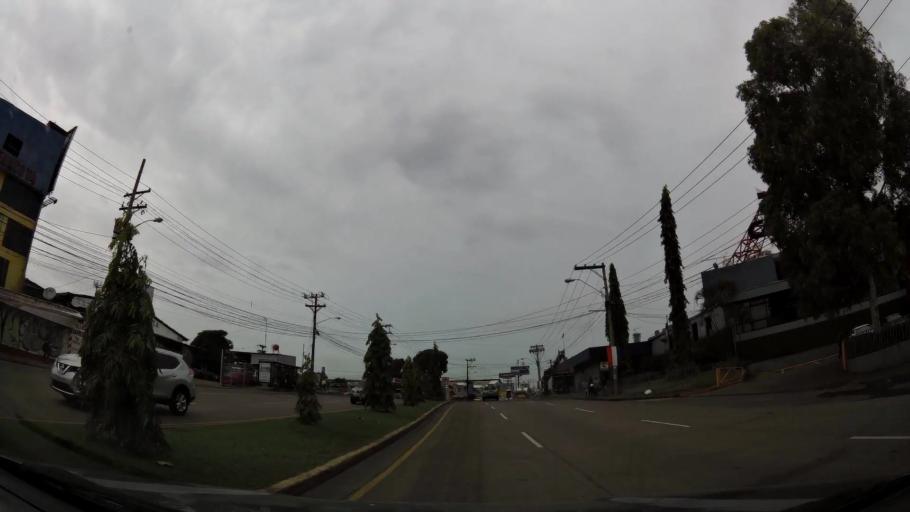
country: PA
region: Panama
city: Panama
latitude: 8.9894
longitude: -79.5333
